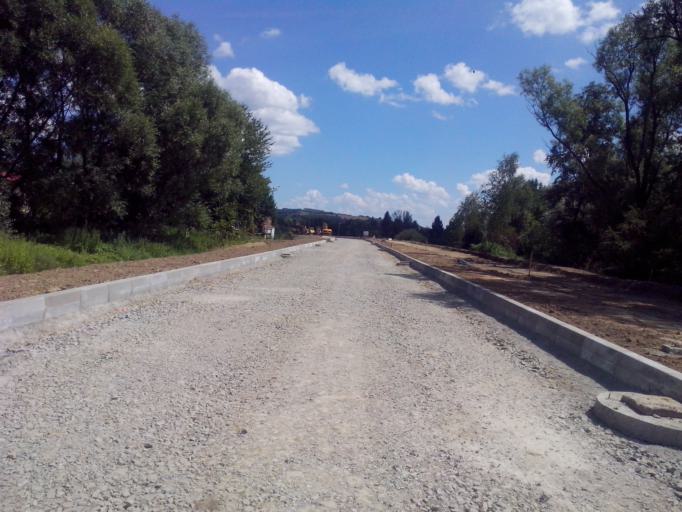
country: PL
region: Subcarpathian Voivodeship
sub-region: Powiat strzyzowski
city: Strzyzow
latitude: 49.8675
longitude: 21.7810
